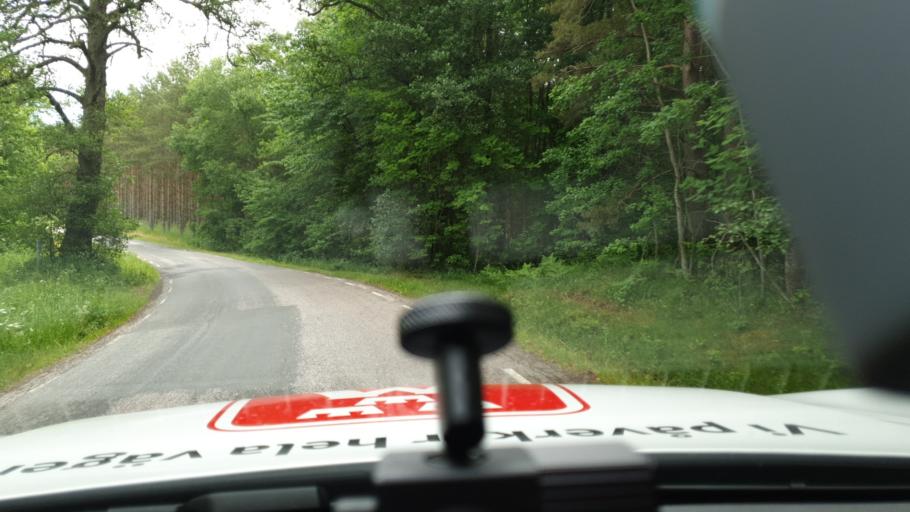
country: SE
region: Vaestra Goetaland
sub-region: Karlsborgs Kommun
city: Molltorp
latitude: 58.4346
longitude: 14.3956
